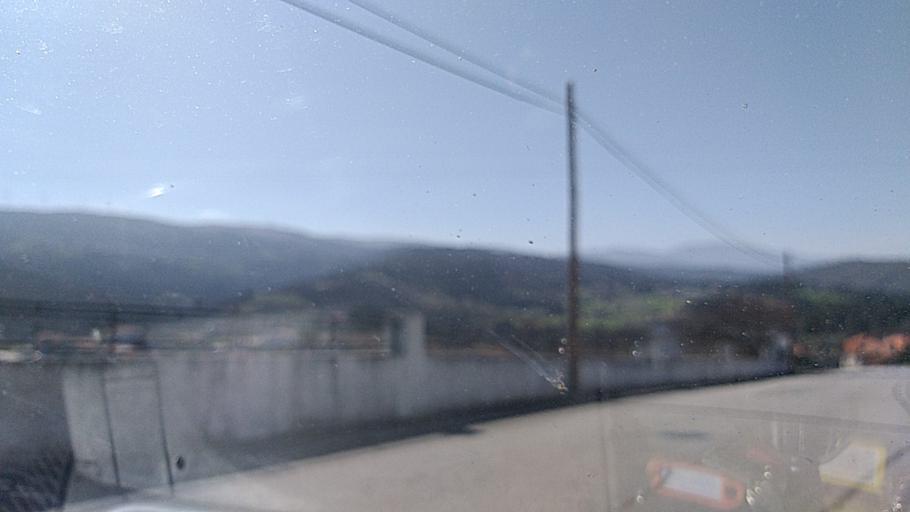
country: PT
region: Guarda
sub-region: Celorico da Beira
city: Celorico da Beira
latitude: 40.6209
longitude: -7.4068
